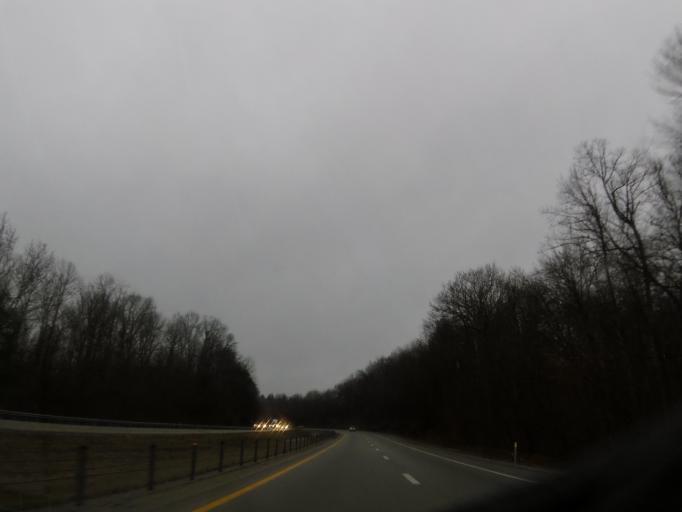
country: US
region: Kentucky
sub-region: Rockcastle County
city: Mount Vernon
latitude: 37.3103
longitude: -84.2907
